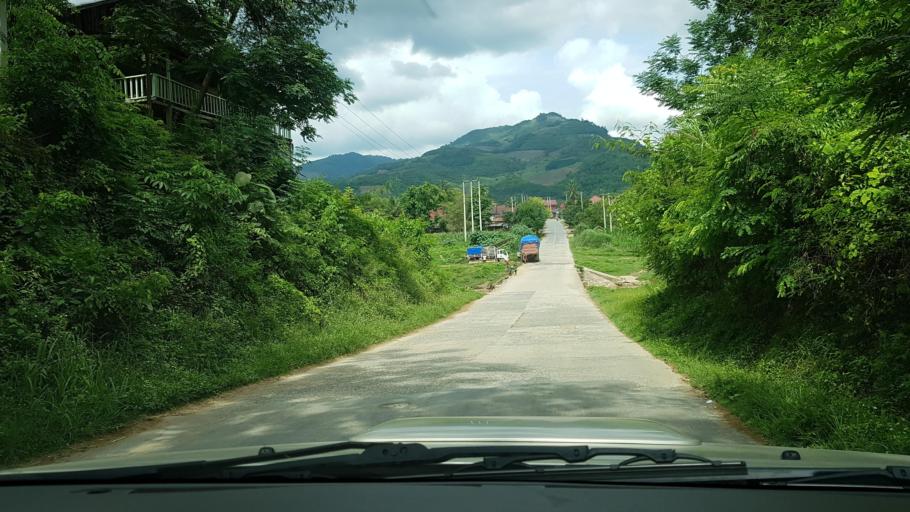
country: LA
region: Loungnamtha
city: Muang Nale
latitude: 20.1544
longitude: 101.4931
